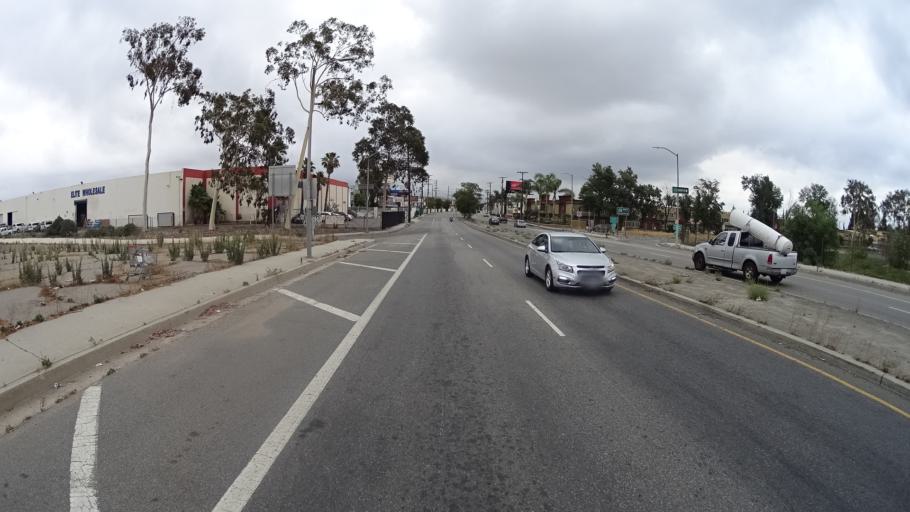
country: US
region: California
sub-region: Los Angeles County
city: North Hollywood
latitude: 34.2013
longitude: -118.4026
